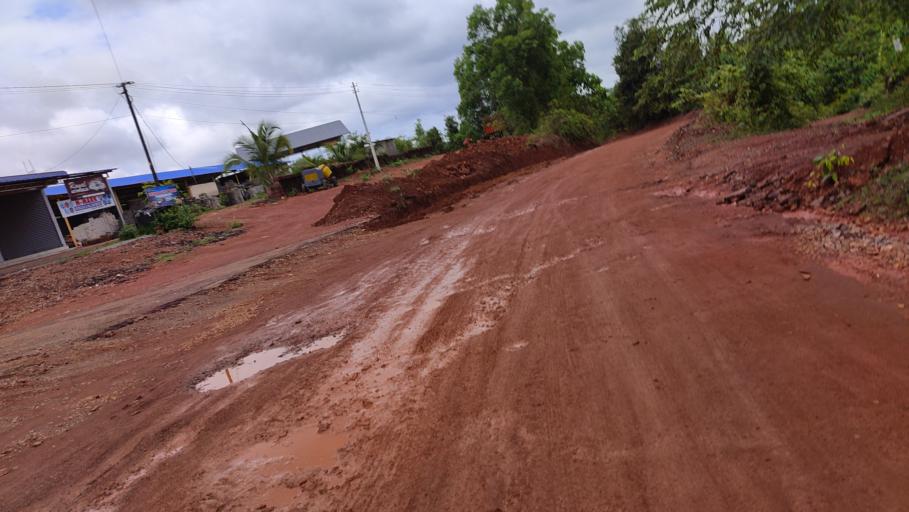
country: IN
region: Kerala
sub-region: Kasaragod District
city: Kasaragod
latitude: 12.5325
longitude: 75.0719
